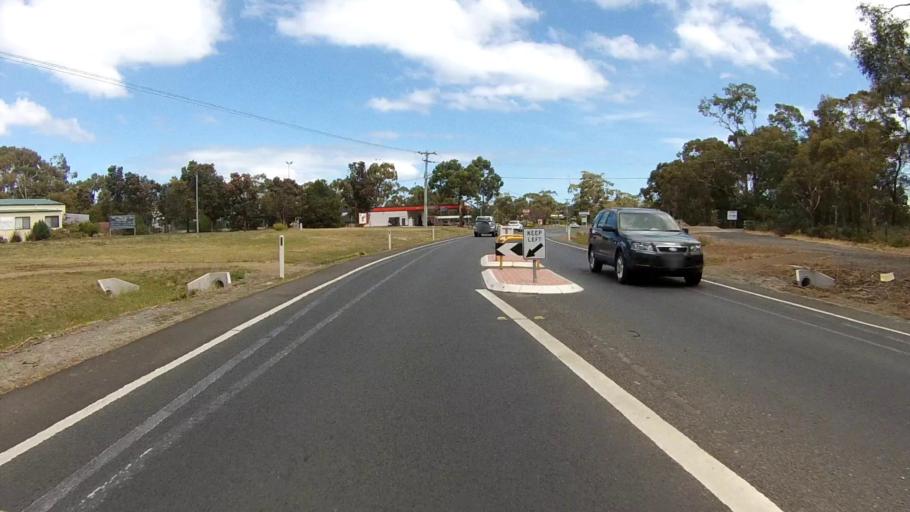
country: AU
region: Tasmania
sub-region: Sorell
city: Sorell
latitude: -42.8479
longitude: 147.6274
